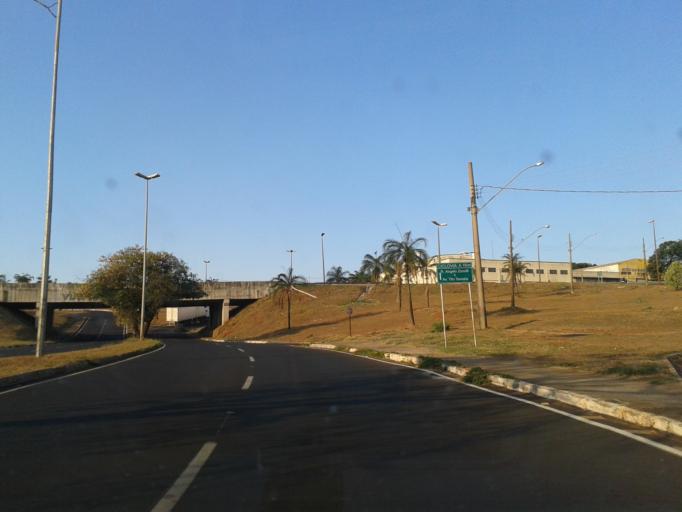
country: BR
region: Minas Gerais
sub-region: Uberlandia
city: Uberlandia
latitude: -18.8944
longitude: -48.2518
